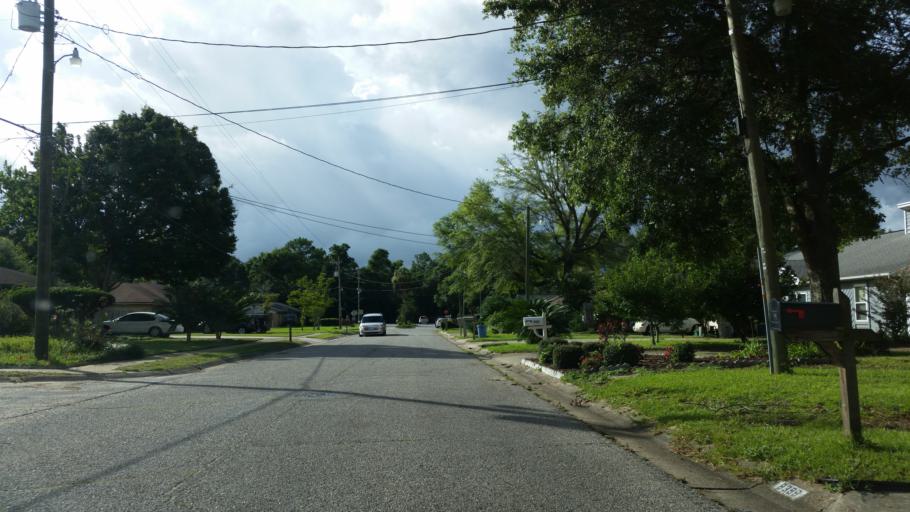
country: US
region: Florida
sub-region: Escambia County
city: Ferry Pass
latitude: 30.5149
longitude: -87.1766
